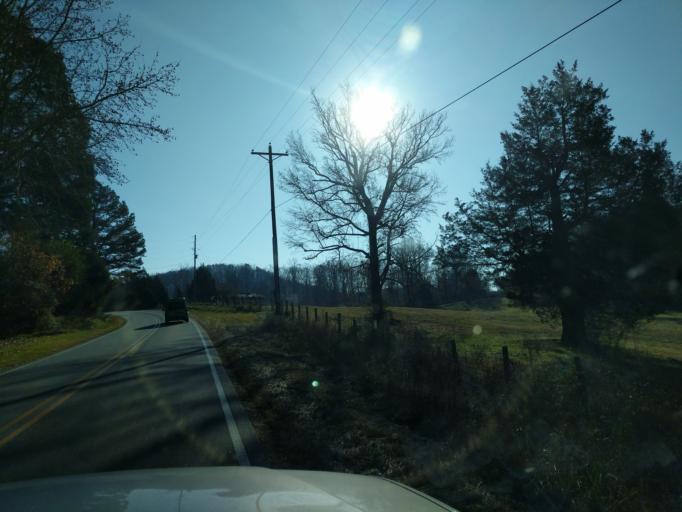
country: US
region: North Carolina
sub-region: Rutherford County
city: Rutherfordton
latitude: 35.2847
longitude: -82.0210
